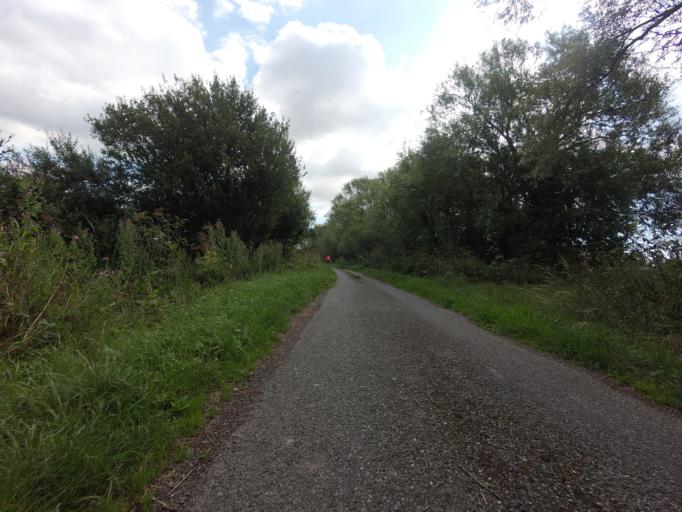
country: GB
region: England
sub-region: Kent
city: Stone
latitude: 51.0547
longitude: 0.7669
